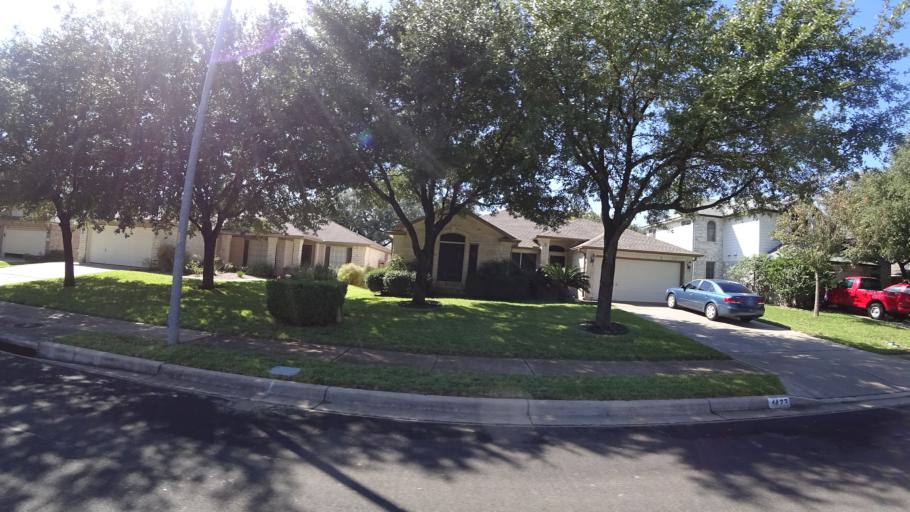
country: US
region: Texas
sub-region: Travis County
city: Shady Hollow
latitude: 30.1941
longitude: -97.8608
